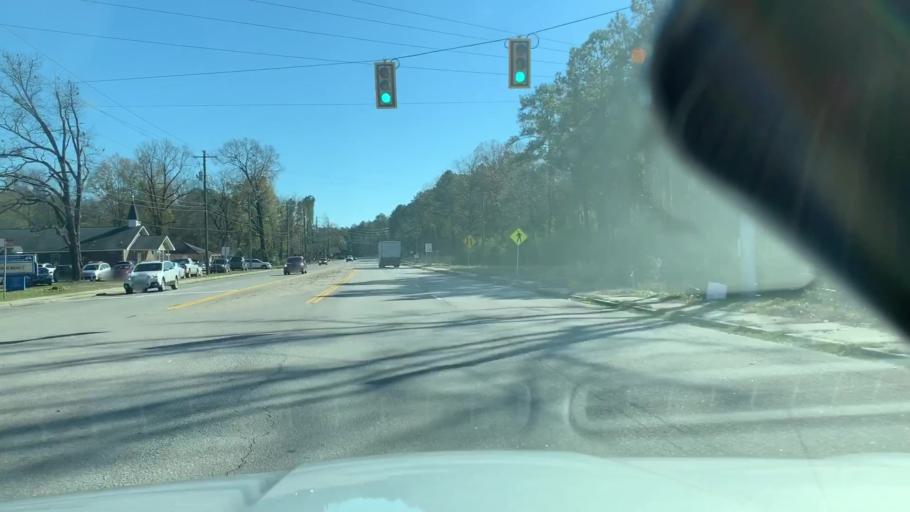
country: US
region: South Carolina
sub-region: Richland County
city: Forest Acres
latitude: 33.9381
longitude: -80.9801
